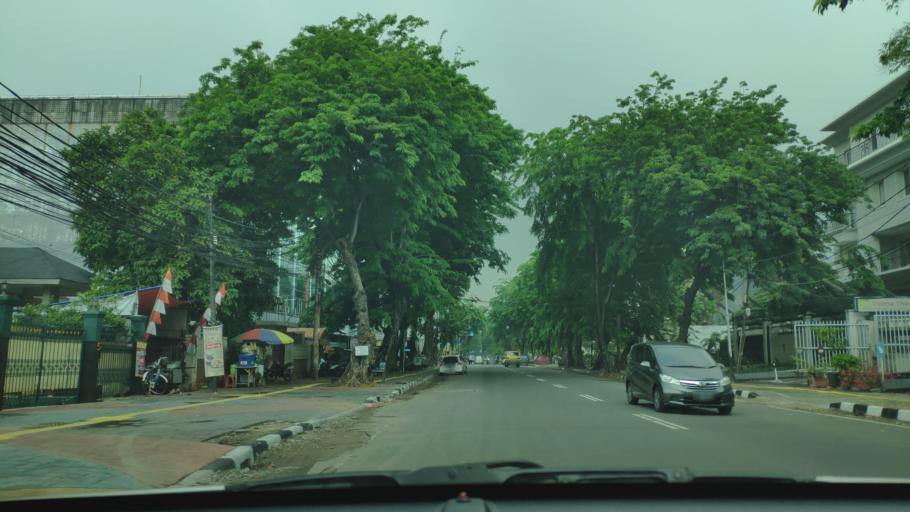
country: ID
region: Jakarta Raya
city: Jakarta
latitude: -6.1664
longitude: 106.8137
